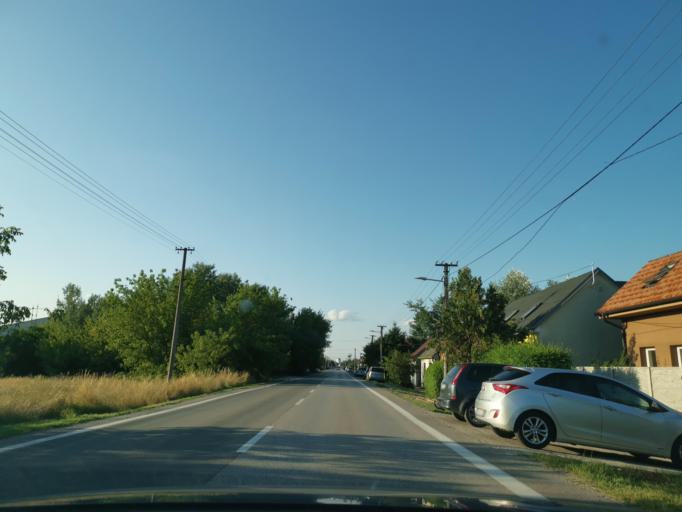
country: SK
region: Bratislavsky
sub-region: Okres Malacky
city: Malacky
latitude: 48.4162
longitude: 17.0195
